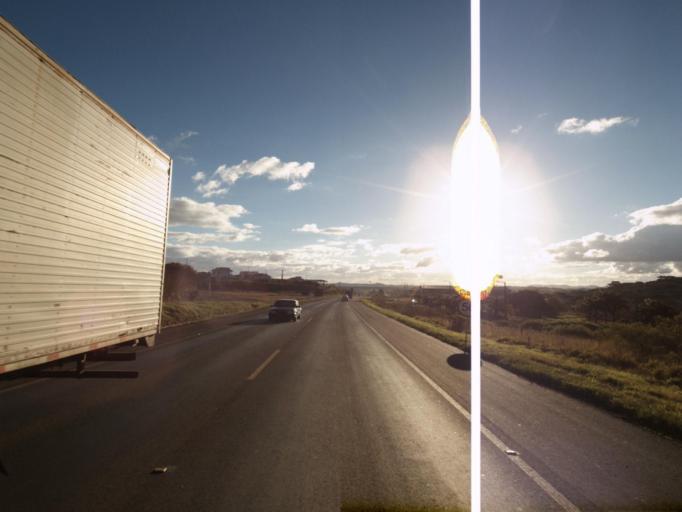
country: BR
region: Santa Catarina
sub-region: Campos Novos
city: Campos Novos
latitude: -27.3905
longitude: -51.2224
